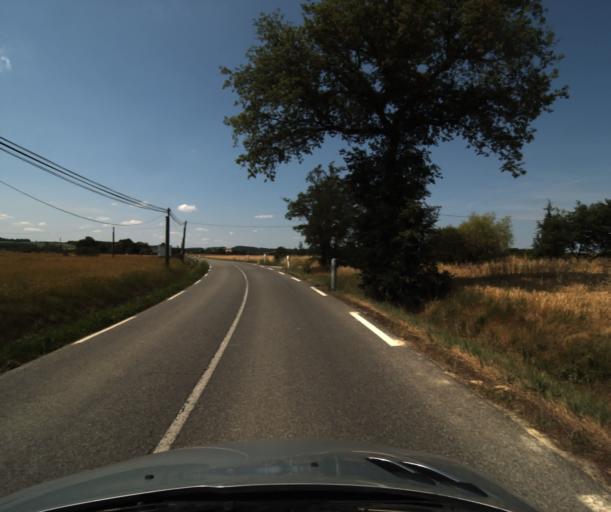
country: FR
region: Midi-Pyrenees
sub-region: Departement de la Haute-Garonne
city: Saint-Lys
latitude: 43.5296
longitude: 1.1717
